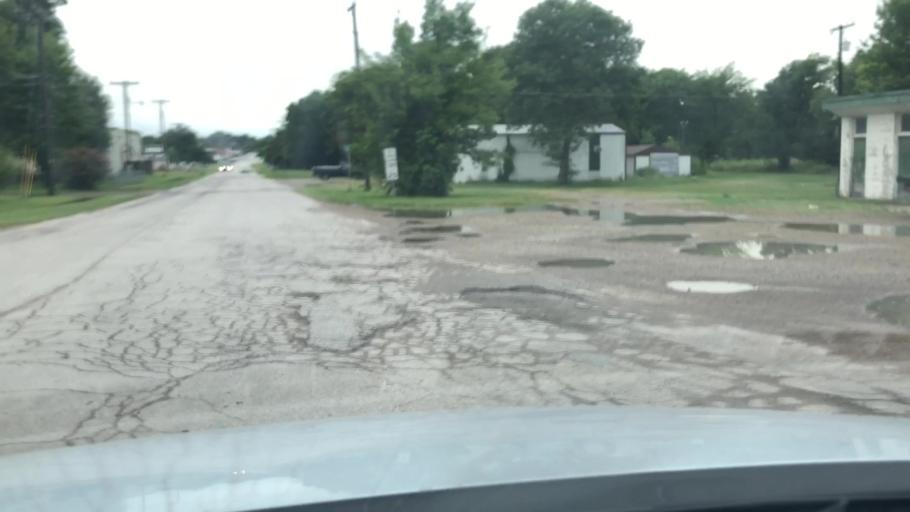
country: US
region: Oklahoma
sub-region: Nowata County
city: Nowata
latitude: 36.7012
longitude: -95.6297
